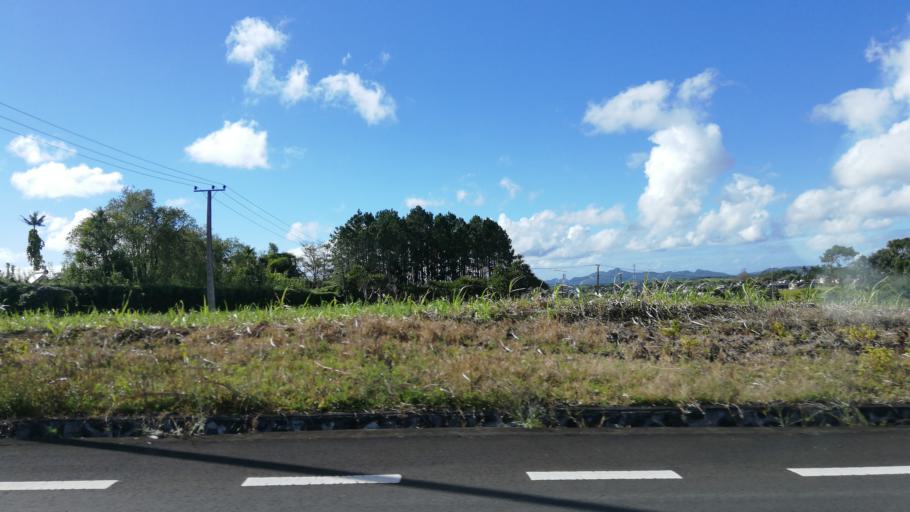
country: MU
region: Moka
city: Quartier Militaire
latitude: -20.2410
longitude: 57.5933
